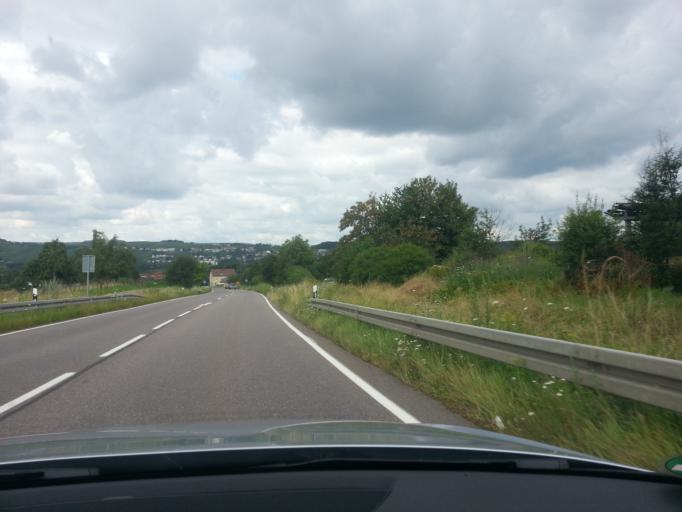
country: LU
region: Grevenmacher
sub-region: Canton de Remich
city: Remich
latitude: 49.5392
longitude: 6.3870
